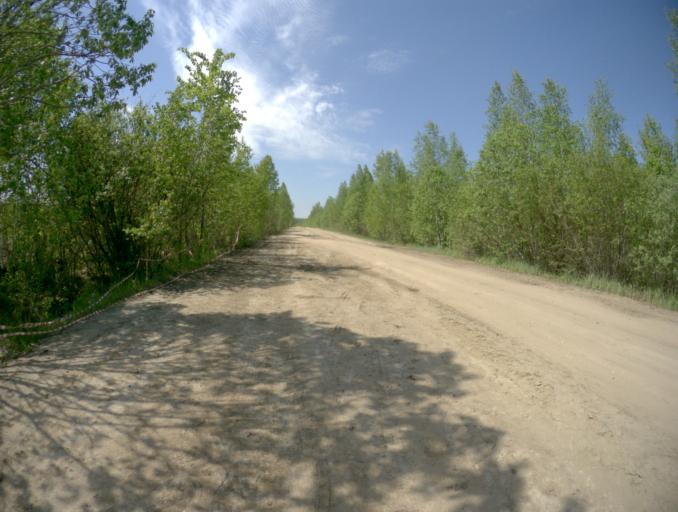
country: RU
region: Vladimir
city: Gusevskiy
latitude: 55.6902
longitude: 40.5311
